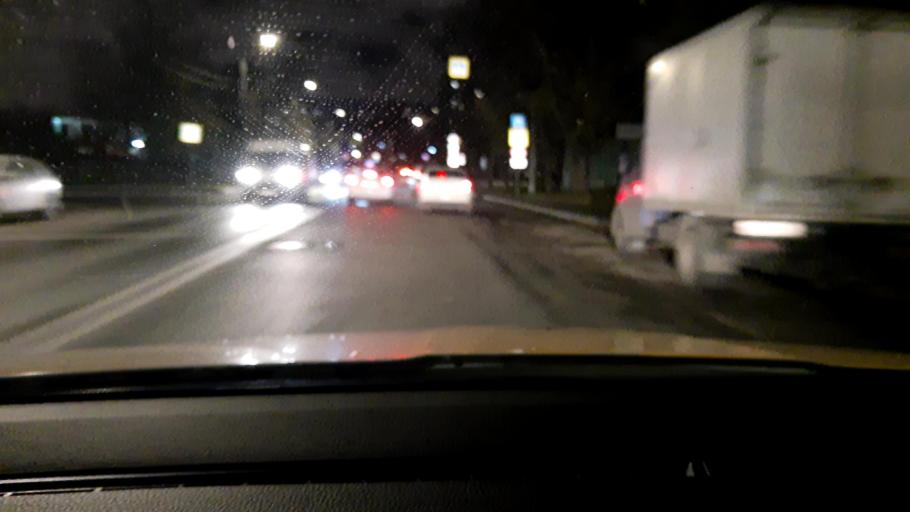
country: RU
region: Moscow
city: Vagonoremont
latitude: 55.8988
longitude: 37.5323
